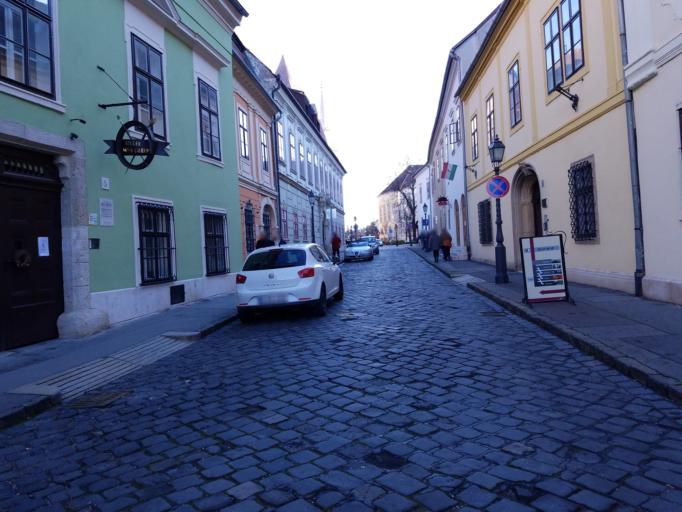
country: HU
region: Budapest
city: Budapest II. keruelet
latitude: 47.5038
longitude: 19.0324
